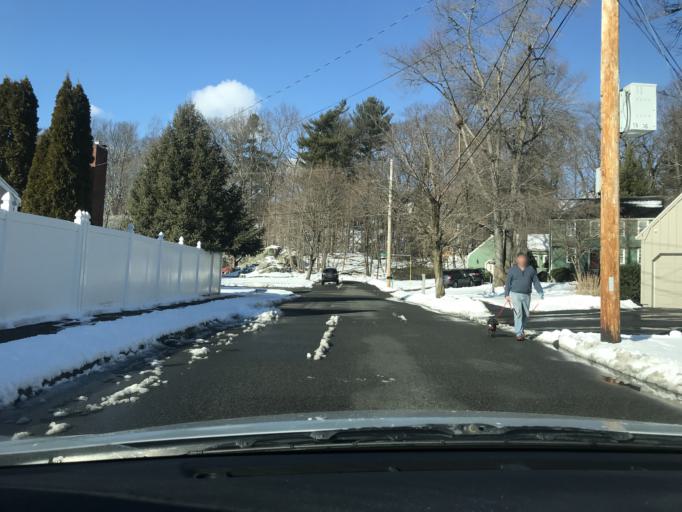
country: US
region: Massachusetts
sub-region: Essex County
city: Saugus
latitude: 42.4804
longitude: -71.0128
